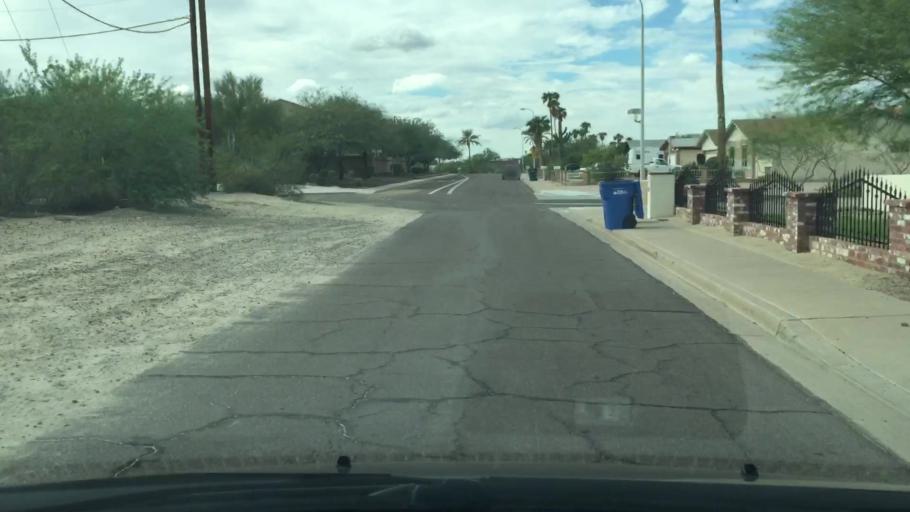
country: US
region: Arizona
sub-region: Maricopa County
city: Guadalupe
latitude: 33.3669
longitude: -112.0419
